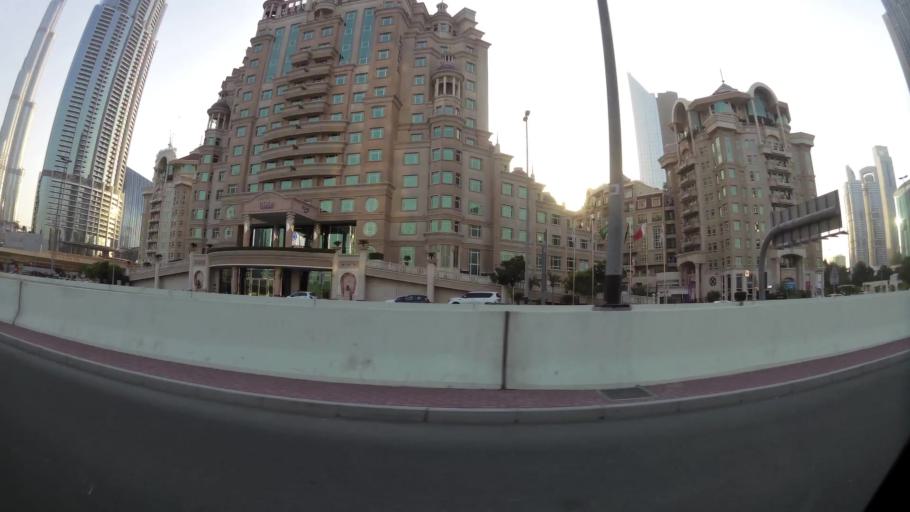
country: AE
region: Dubai
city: Dubai
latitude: 25.2029
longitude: 55.2787
